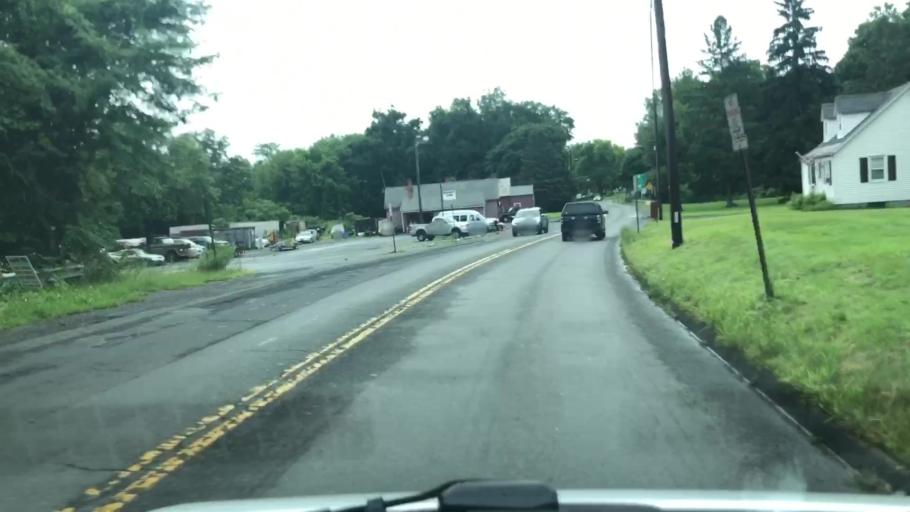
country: US
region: Massachusetts
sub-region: Hampshire County
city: Northampton
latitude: 42.3360
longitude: -72.6241
